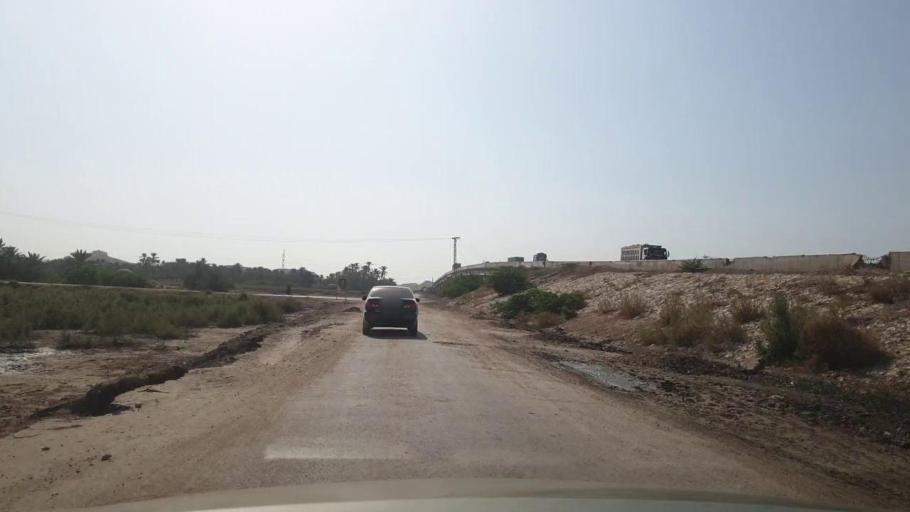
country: PK
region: Sindh
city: Rohri
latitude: 27.6664
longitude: 68.8765
